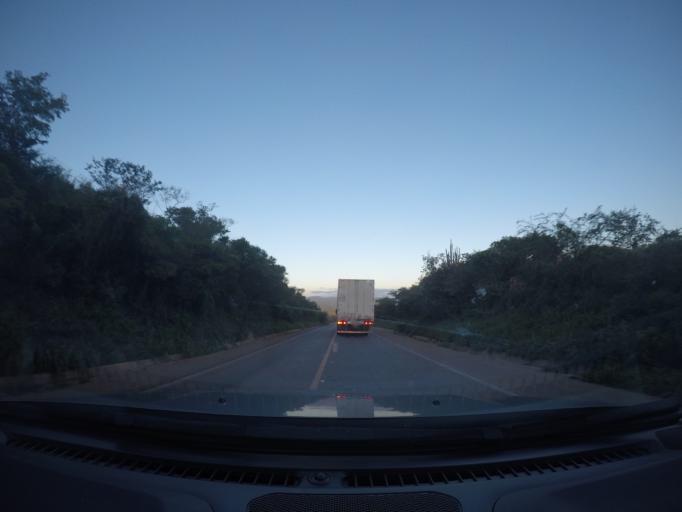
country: BR
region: Bahia
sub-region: Seabra
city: Seabra
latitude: -12.4131
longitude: -41.9766
